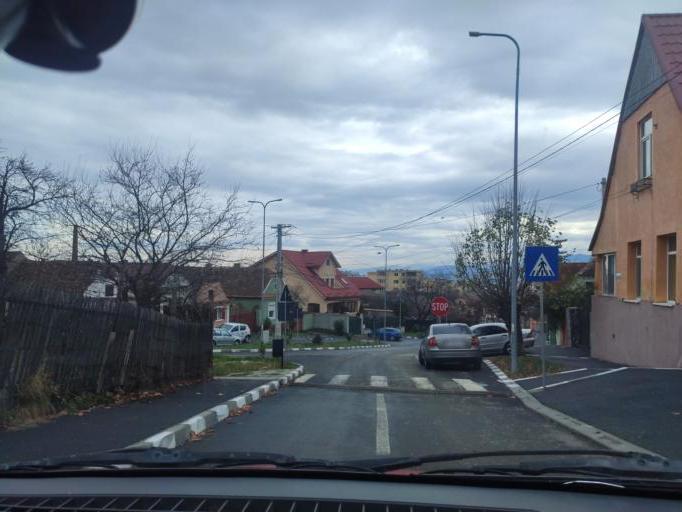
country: RO
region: Brasov
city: Codlea
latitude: 45.7046
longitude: 25.4397
